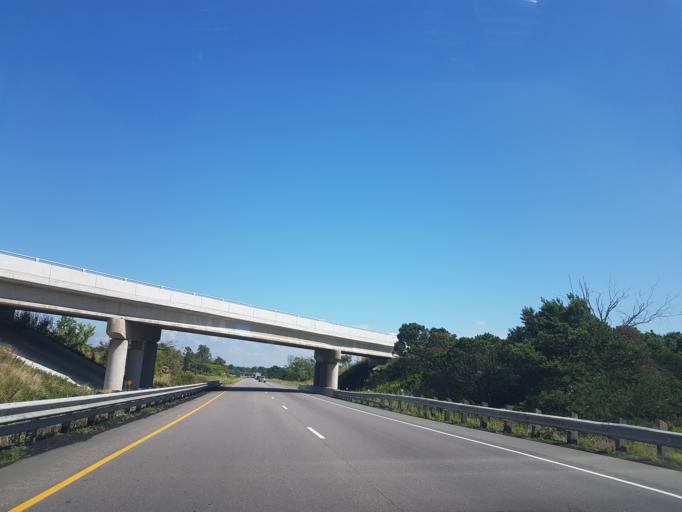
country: CA
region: Ontario
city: Gananoque
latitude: 44.3433
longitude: -76.1481
